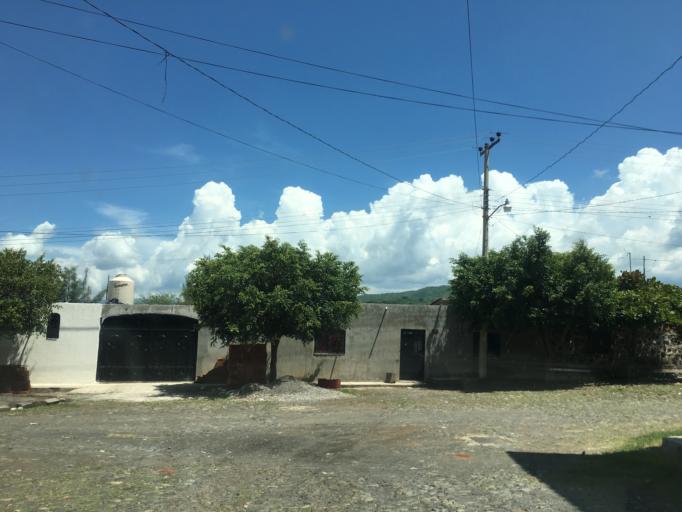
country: MX
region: Nayarit
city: Ixtlan del Rio
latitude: 21.0363
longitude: -104.3505
